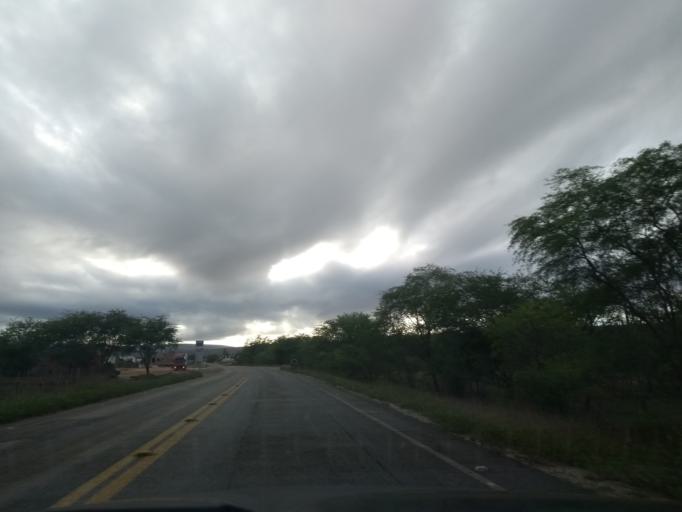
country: BR
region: Bahia
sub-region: Ituacu
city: Ituacu
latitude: -13.7660
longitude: -41.0399
